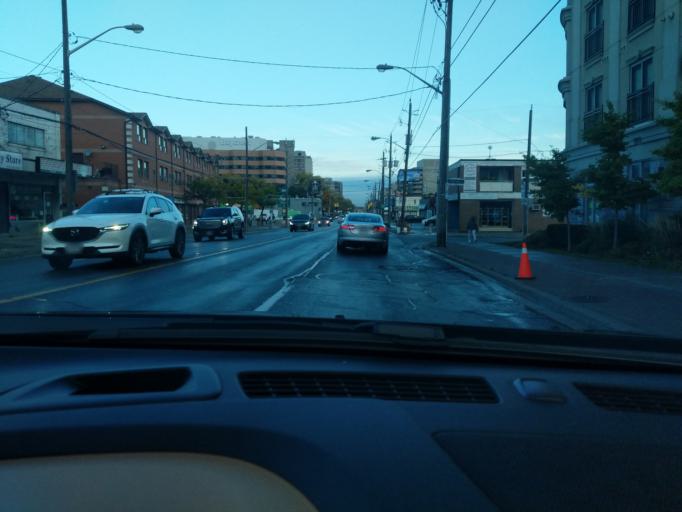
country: CA
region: Ontario
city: Toronto
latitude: 43.7279
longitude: -79.4317
